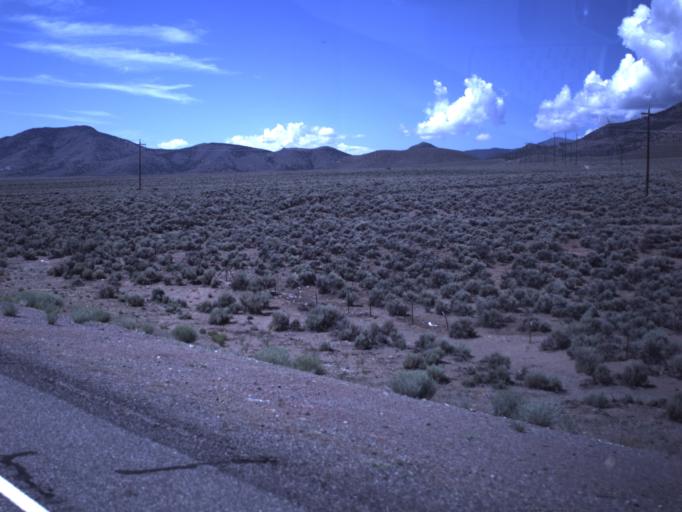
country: US
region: Utah
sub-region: Piute County
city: Junction
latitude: 38.2912
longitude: -112.2254
